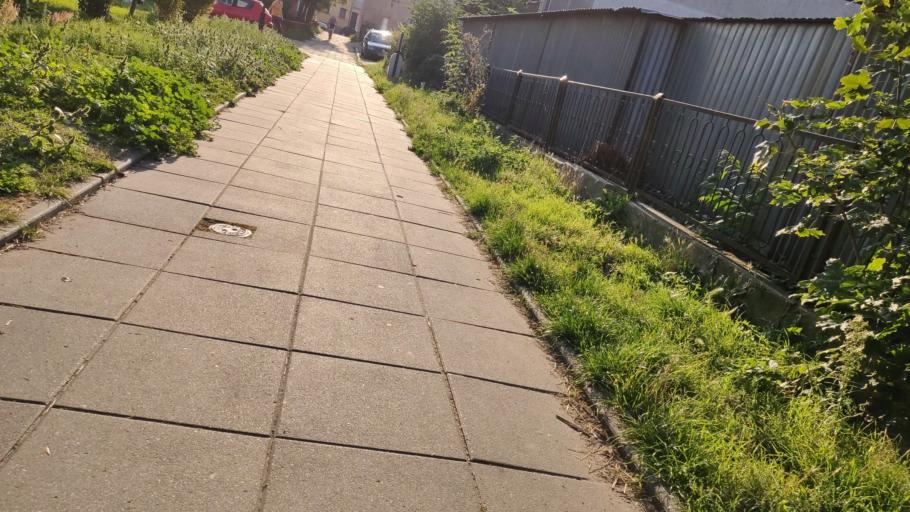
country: PL
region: Kujawsko-Pomorskie
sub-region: Powiat zninski
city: Znin
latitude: 52.8497
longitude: 17.7235
